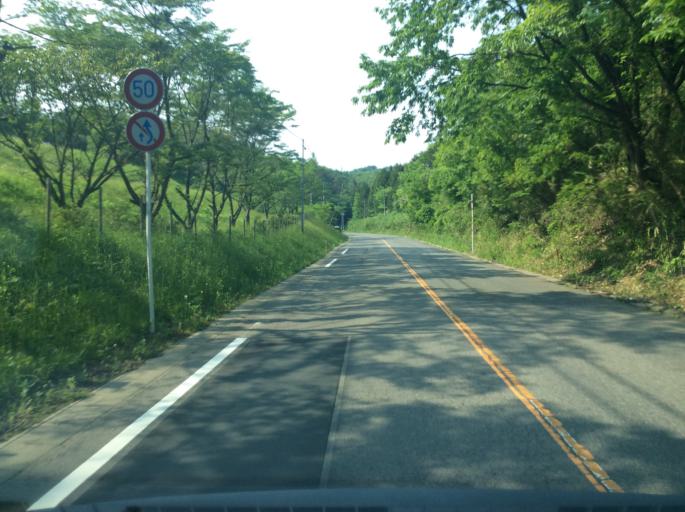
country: JP
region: Tochigi
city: Kuroiso
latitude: 37.0753
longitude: 140.2224
